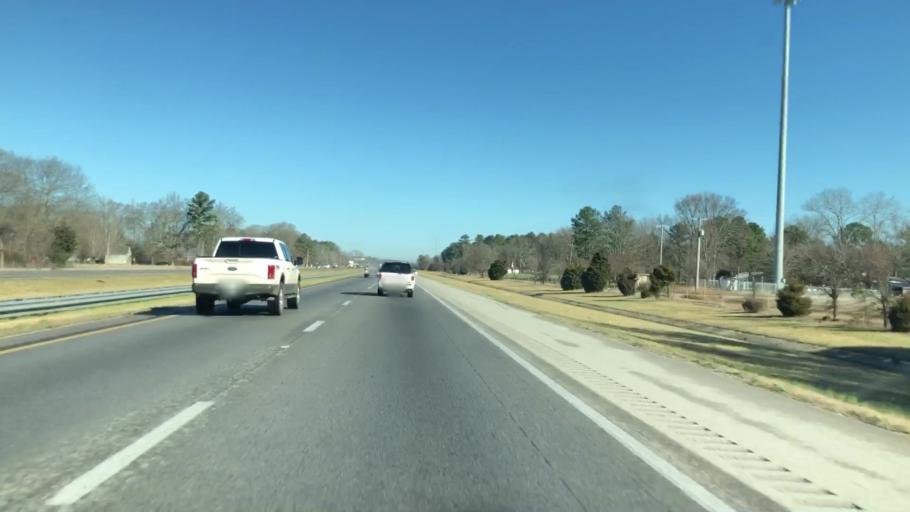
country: US
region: Alabama
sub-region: Limestone County
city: Athens
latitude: 34.8644
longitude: -86.9250
